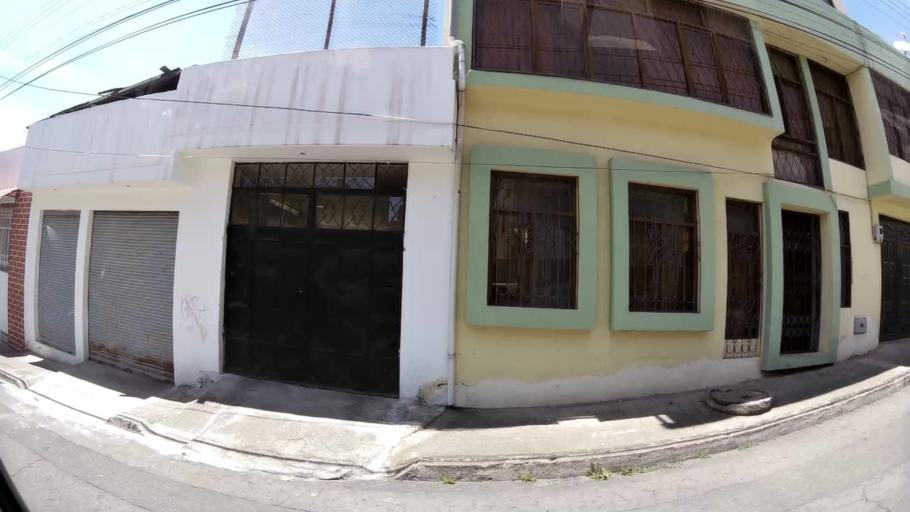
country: EC
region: Chimborazo
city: Riobamba
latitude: -1.6602
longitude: -78.6598
